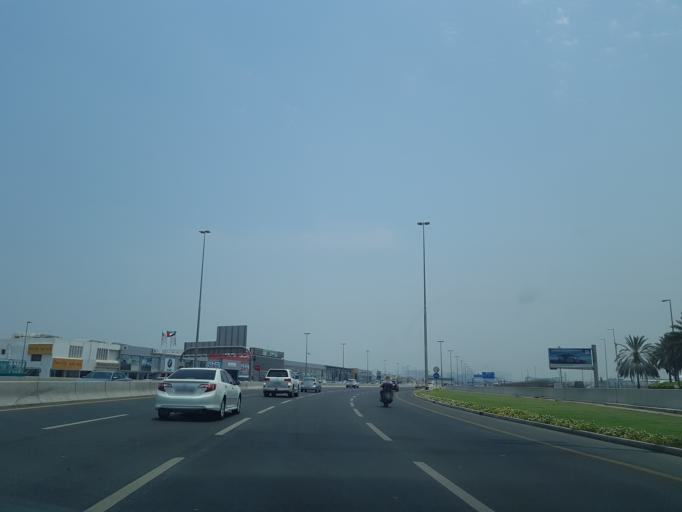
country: AE
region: Ash Shariqah
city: Sharjah
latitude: 25.2639
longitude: 55.3370
